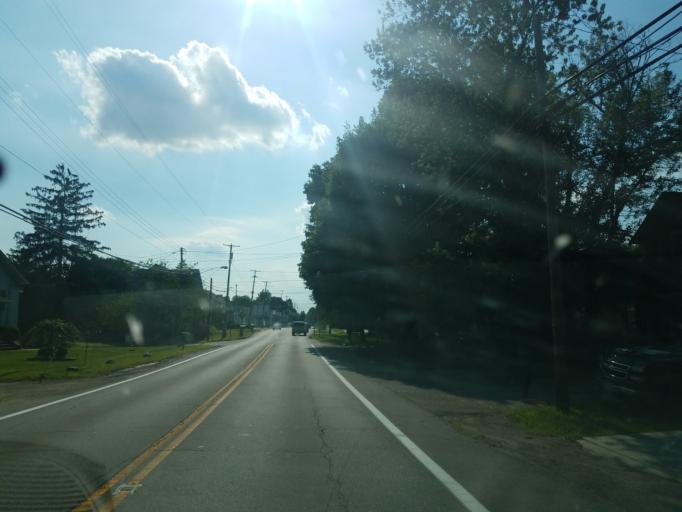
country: US
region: Ohio
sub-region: Stark County
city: Uniontown
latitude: 40.9763
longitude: -81.4050
